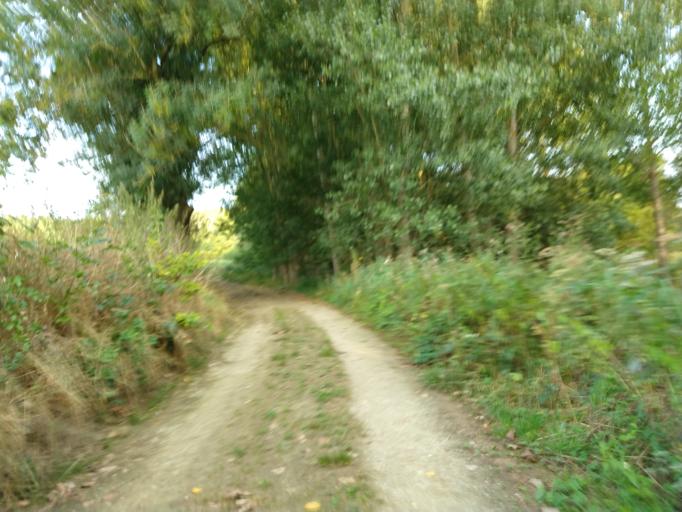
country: BE
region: Flanders
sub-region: Provincie Vlaams-Brabant
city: Boutersem
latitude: 50.8038
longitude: 4.8491
